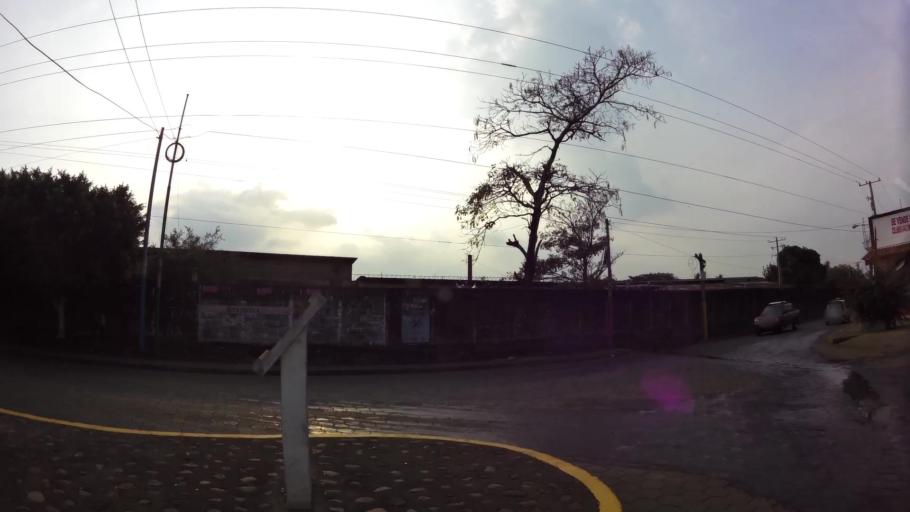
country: NI
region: Masaya
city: Masaya
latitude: 11.9832
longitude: -86.0860
